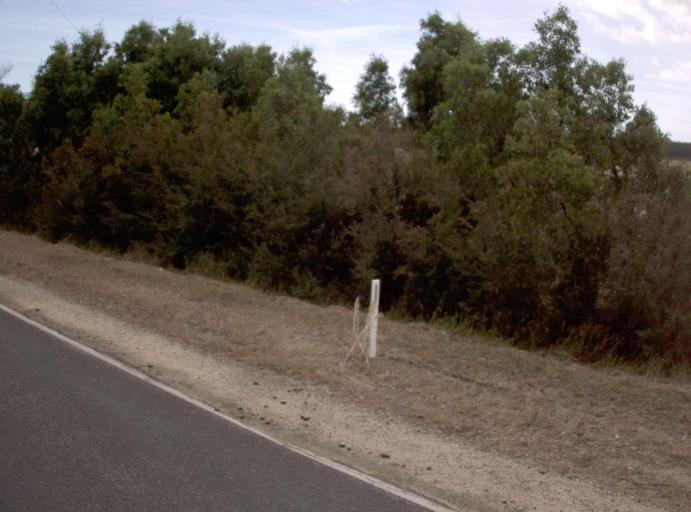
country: AU
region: Victoria
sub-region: Wellington
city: Sale
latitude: -38.2019
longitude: 147.0972
